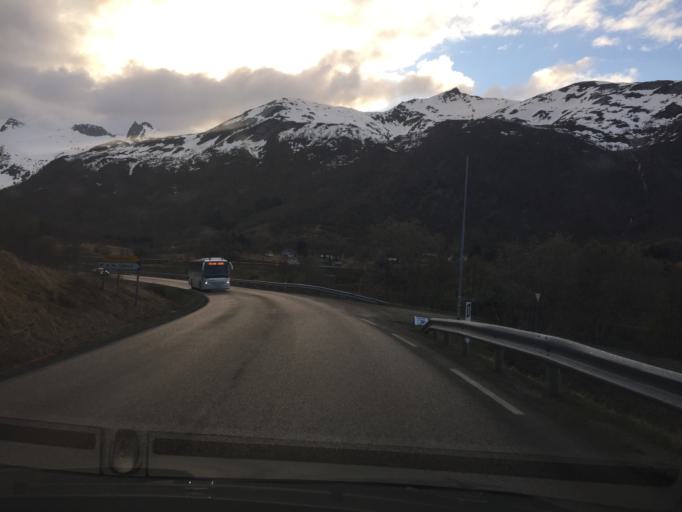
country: NO
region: Nordland
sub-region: Vagan
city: Svolvaer
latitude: 68.3238
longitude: 14.6986
